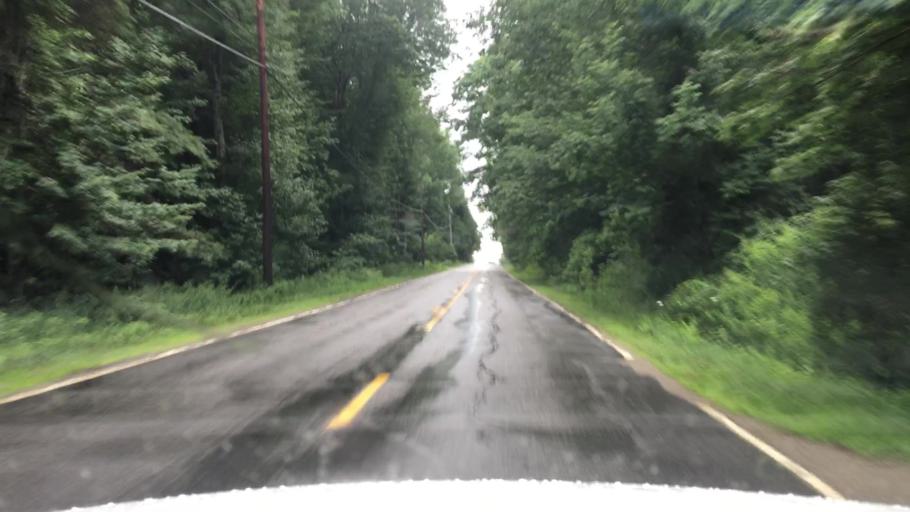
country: US
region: Maine
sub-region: Kennebec County
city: Winthrop
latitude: 44.2949
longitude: -69.9286
